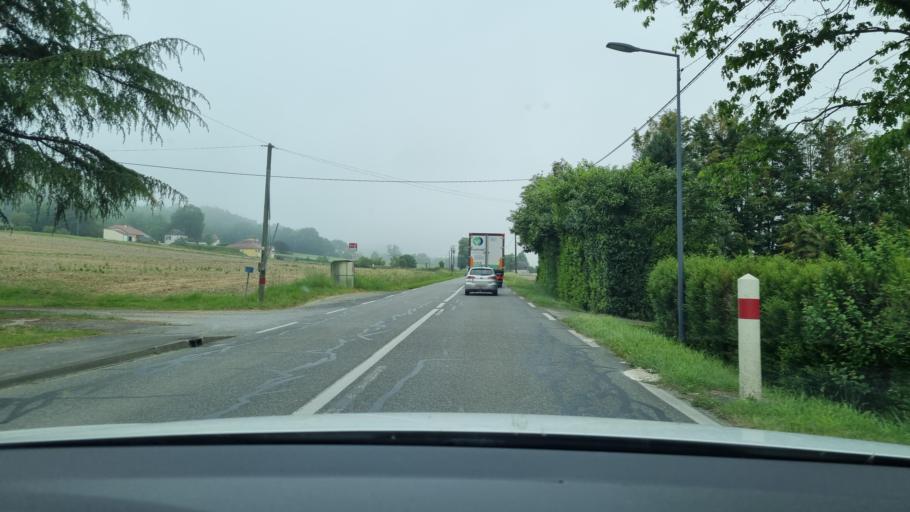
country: FR
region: Aquitaine
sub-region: Departement des Pyrenees-Atlantiques
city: Orthez
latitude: 43.5044
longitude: -0.7413
